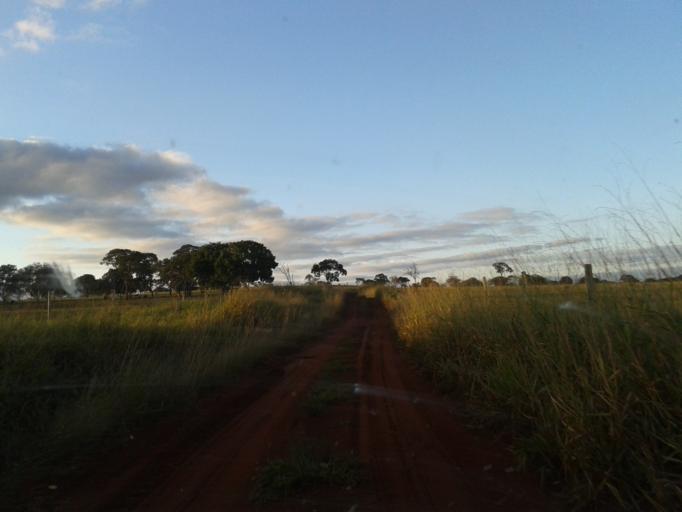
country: BR
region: Minas Gerais
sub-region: Campina Verde
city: Campina Verde
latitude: -19.4990
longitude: -49.6801
